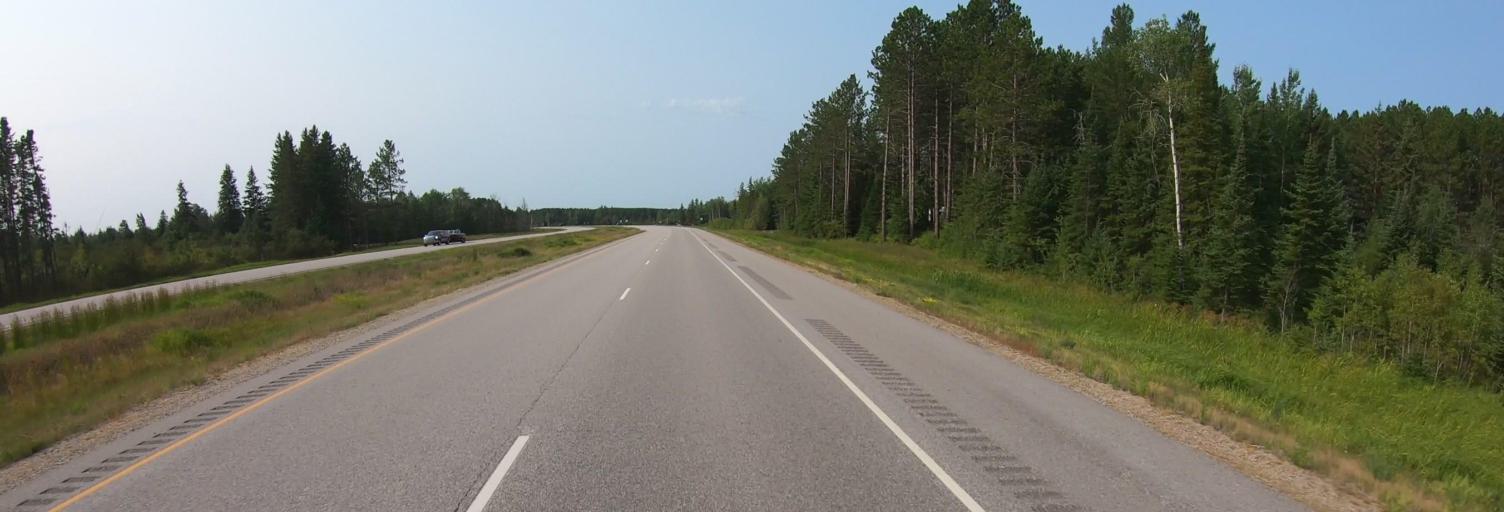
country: US
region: Minnesota
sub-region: Saint Louis County
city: Mountain Iron
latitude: 47.7403
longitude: -92.6492
